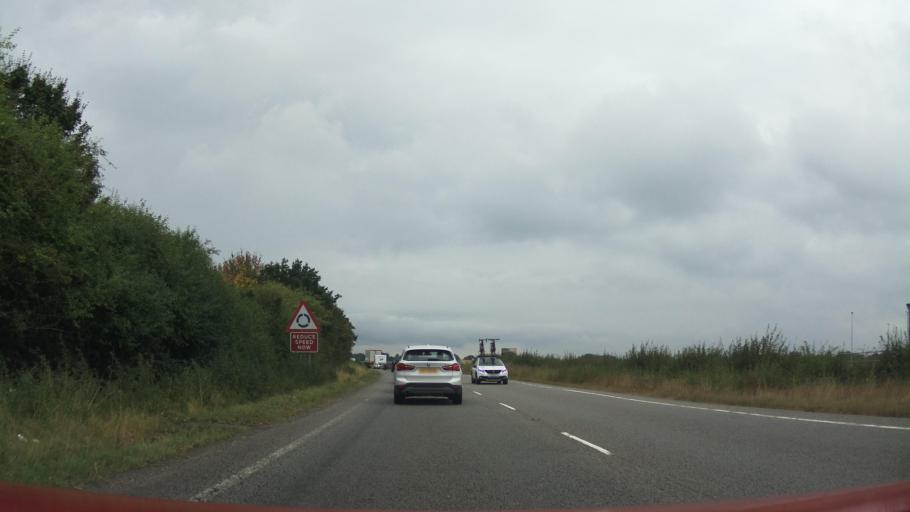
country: GB
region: England
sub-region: Nottinghamshire
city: South Collingham
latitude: 53.0934
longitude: -0.7725
